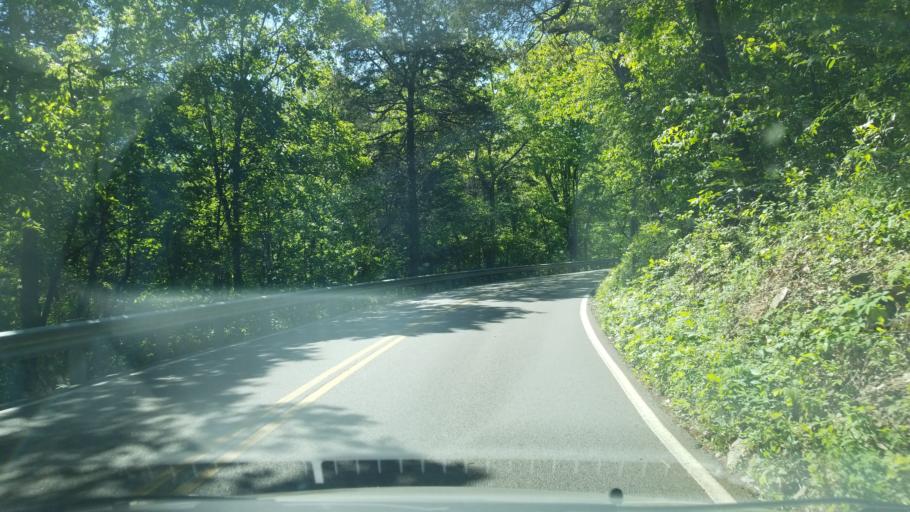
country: US
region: Tennessee
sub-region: Hamilton County
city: Middle Valley
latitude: 35.1698
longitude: -85.1750
